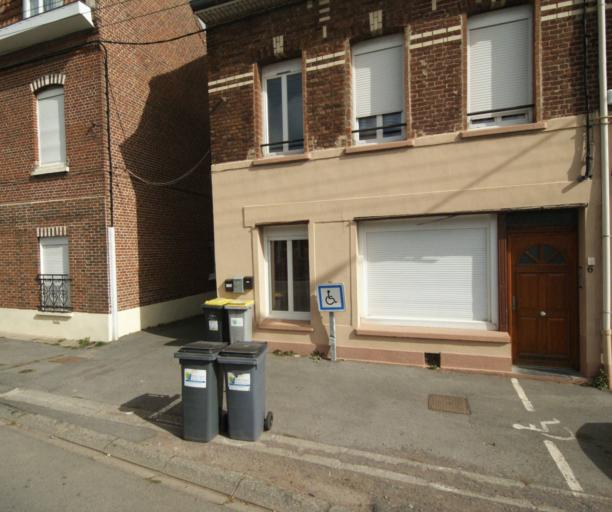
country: FR
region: Nord-Pas-de-Calais
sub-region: Departement du Nord
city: La Bassee
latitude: 50.5267
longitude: 2.8038
